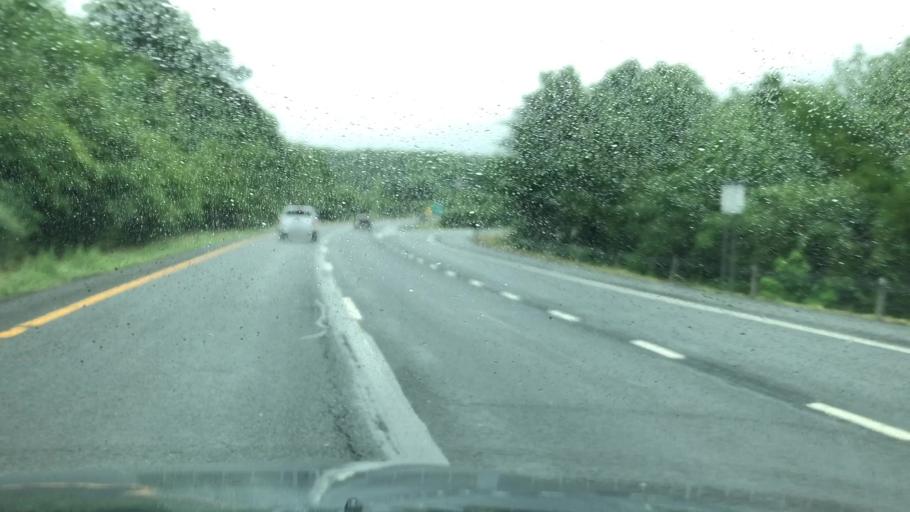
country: US
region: New York
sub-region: Orange County
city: Port Jervis
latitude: 41.3543
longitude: -74.6754
